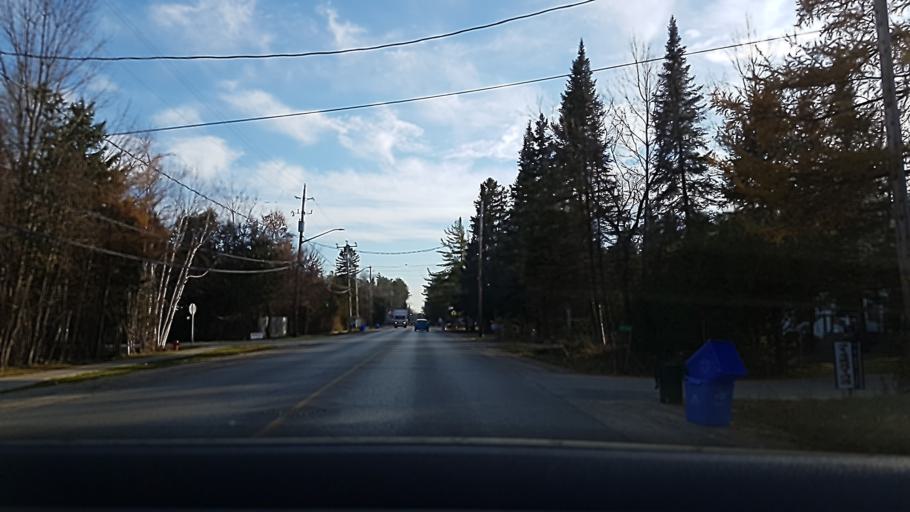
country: CA
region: Ontario
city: Innisfil
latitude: 44.3309
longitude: -79.5435
